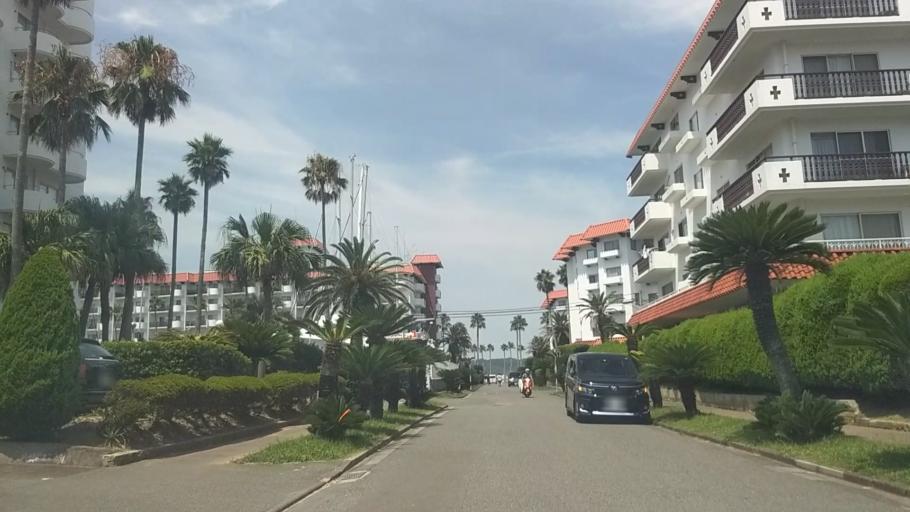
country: JP
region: Kanagawa
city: Kamakura
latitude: 35.2972
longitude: 139.5534
